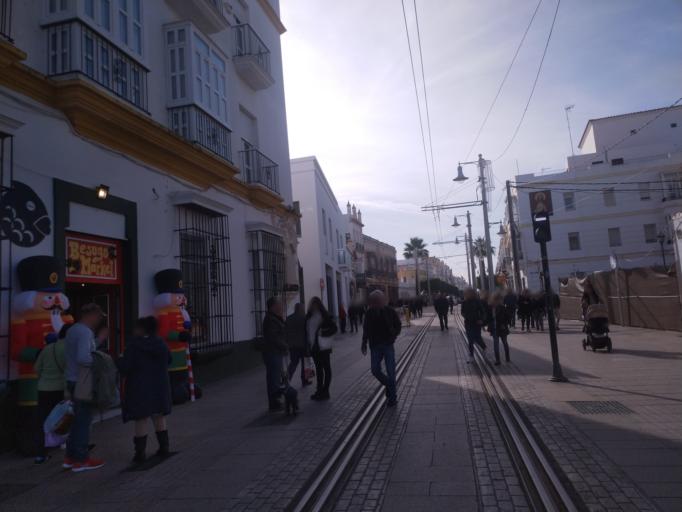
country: ES
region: Andalusia
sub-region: Provincia de Cadiz
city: San Fernando
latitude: 36.4626
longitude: -6.1999
